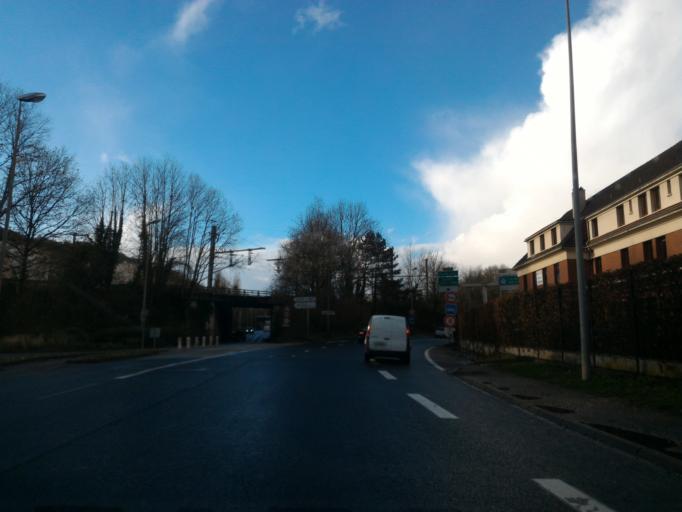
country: FR
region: Haute-Normandie
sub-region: Departement de la Seine-Maritime
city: Bihorel
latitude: 49.4369
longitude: 1.1264
